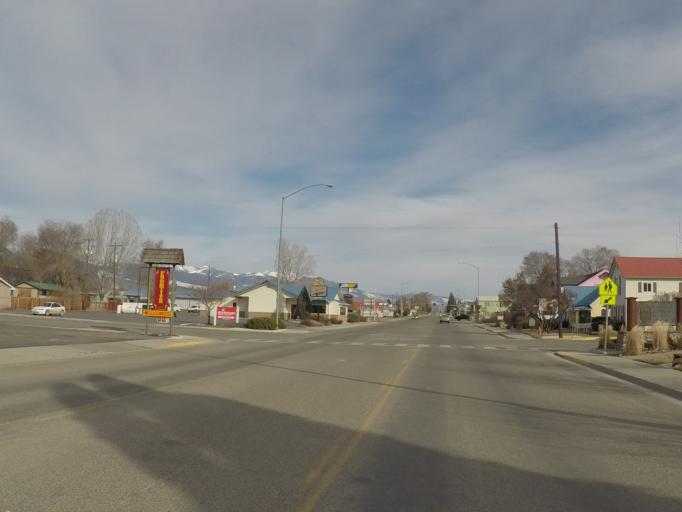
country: US
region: Idaho
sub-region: Lemhi County
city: Salmon
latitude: 45.1744
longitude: -113.8907
